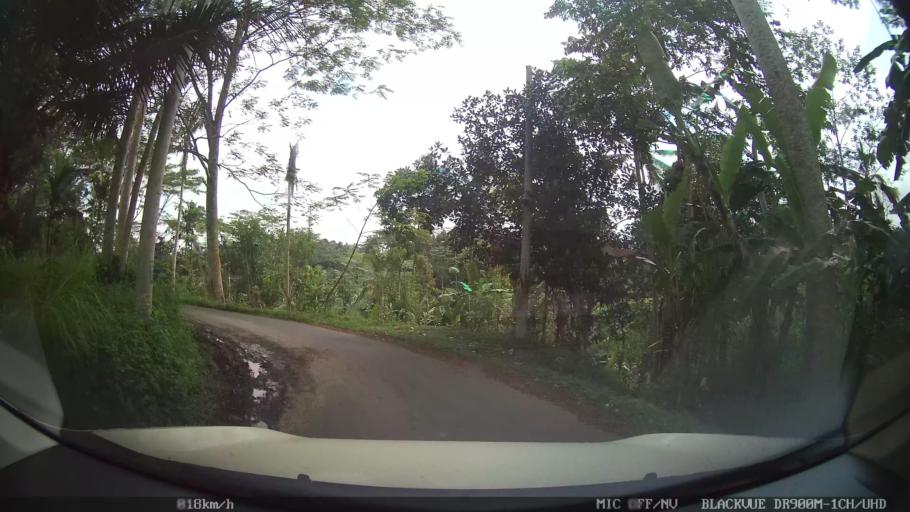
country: ID
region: Bali
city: Banjar Petak
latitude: -8.4455
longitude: 115.3281
